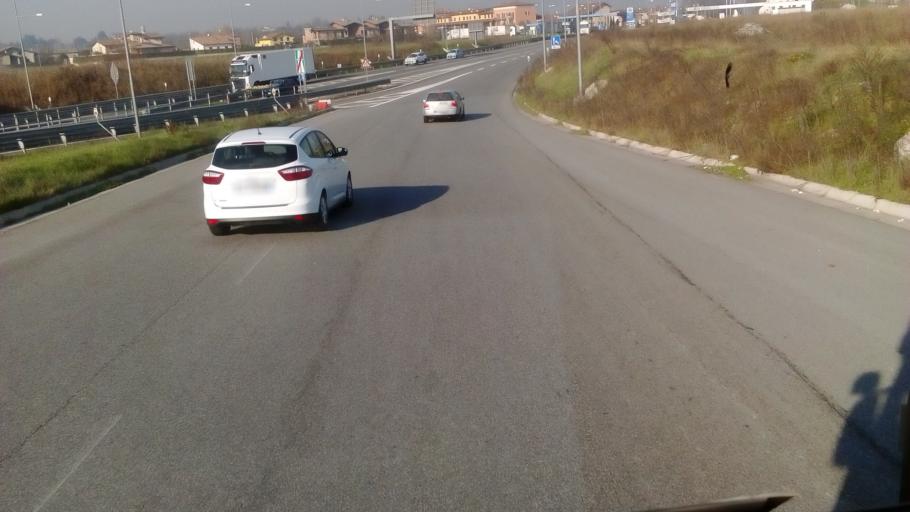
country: IT
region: Lombardy
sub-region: Provincia di Brescia
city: Castenedolo
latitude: 45.4587
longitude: 10.3199
